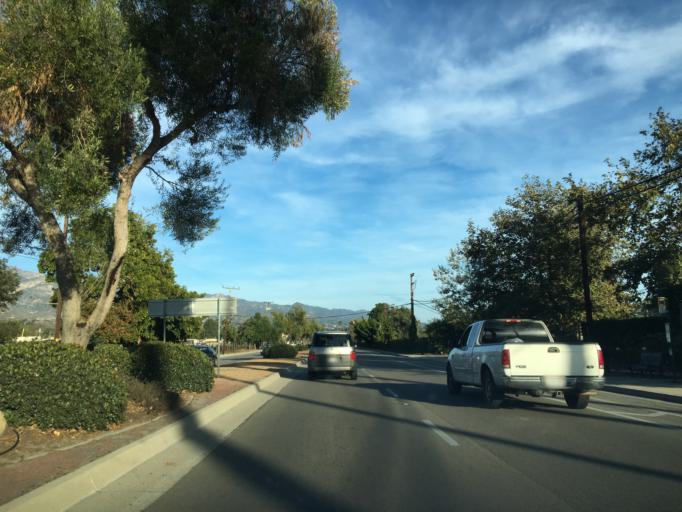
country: US
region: California
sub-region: Santa Barbara County
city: Goleta
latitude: 34.4354
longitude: -119.7954
